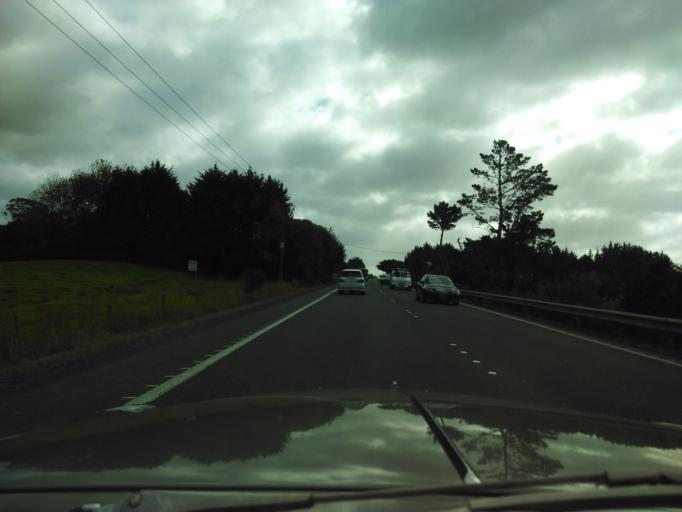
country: NZ
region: Auckland
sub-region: Auckland
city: Warkworth
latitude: -36.4732
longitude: 174.6509
